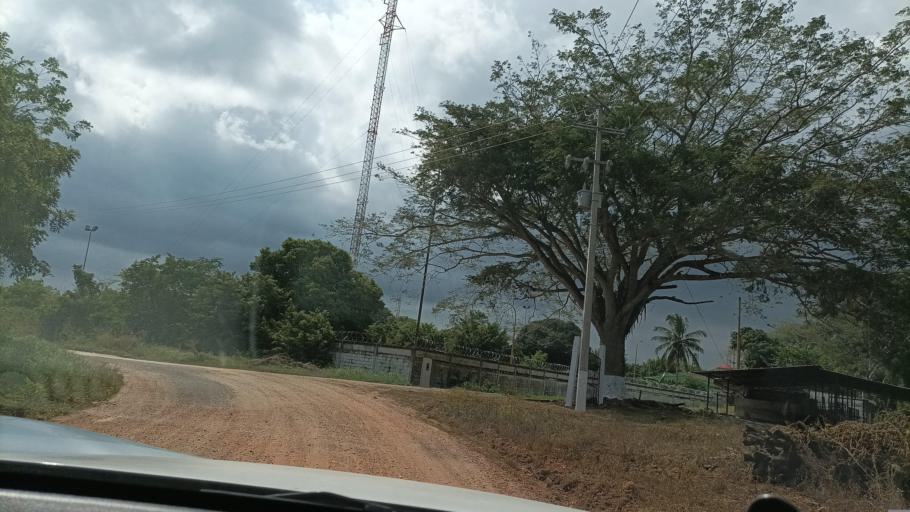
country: MX
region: Veracruz
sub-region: Chinameca
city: Chacalapa
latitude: 18.0803
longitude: -94.6899
